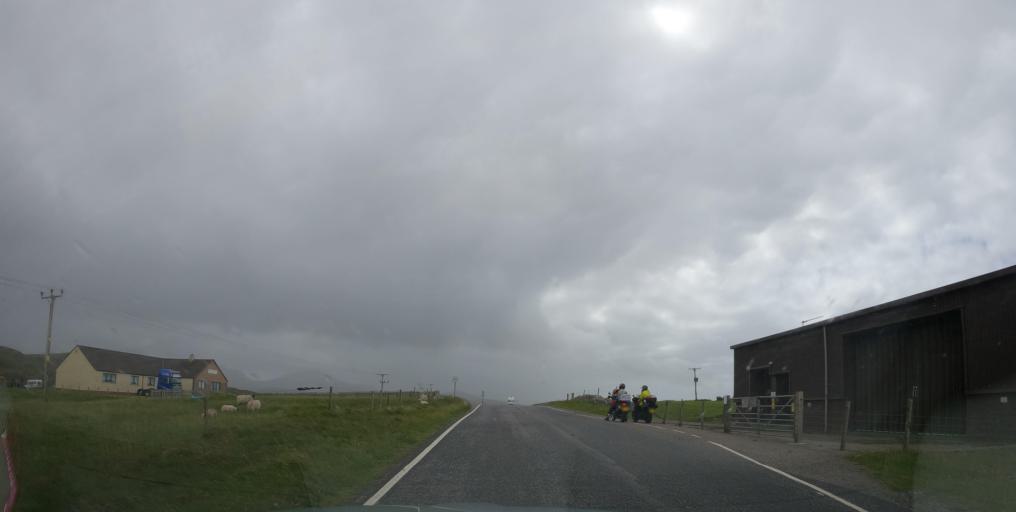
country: GB
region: Scotland
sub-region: Eilean Siar
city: Isle of South Uist
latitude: 57.3364
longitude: -7.3637
